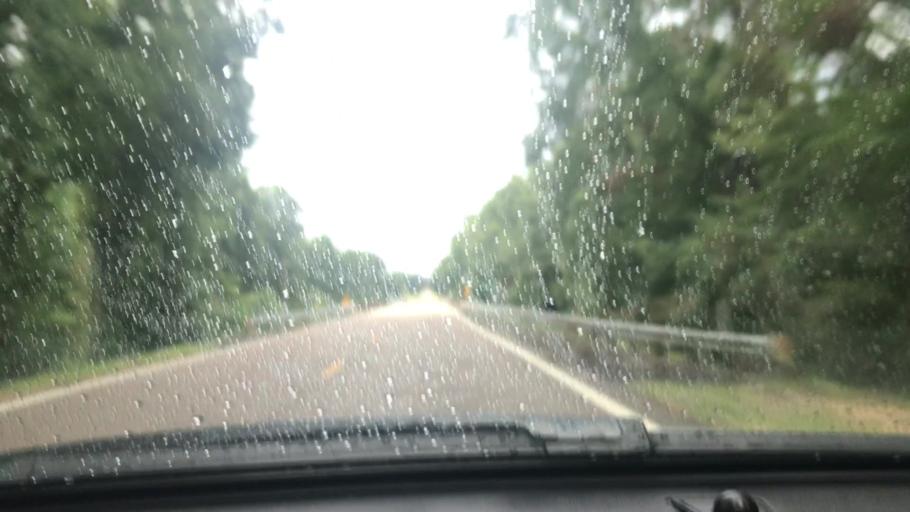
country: US
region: Mississippi
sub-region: Pike County
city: Summit
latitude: 31.3563
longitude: -90.6142
